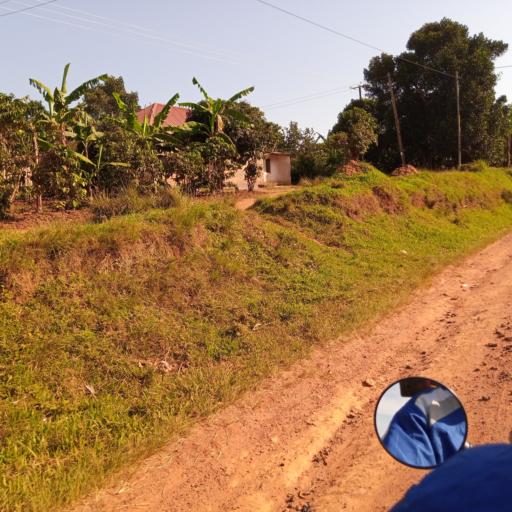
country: UG
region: Central Region
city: Masaka
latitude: -0.4568
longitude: 31.6662
